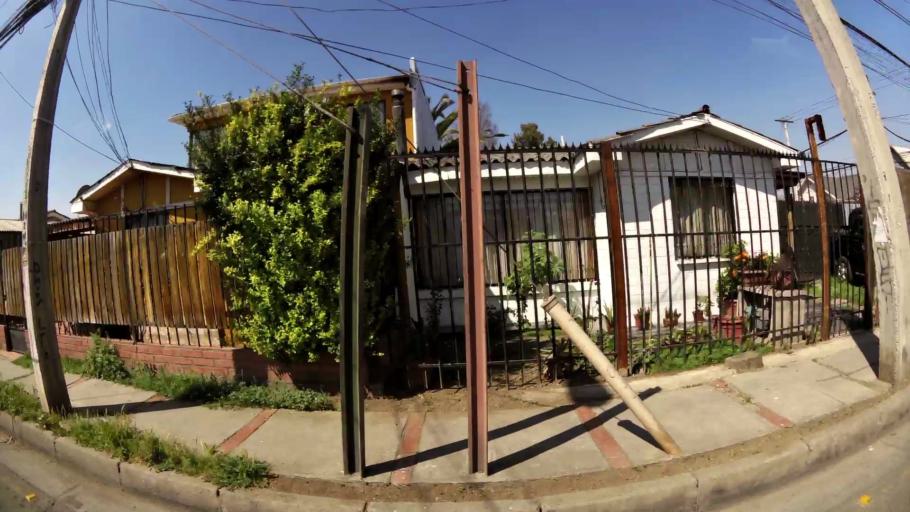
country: CL
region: Santiago Metropolitan
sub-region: Provincia de Santiago
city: Lo Prado
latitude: -33.3641
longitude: -70.7243
